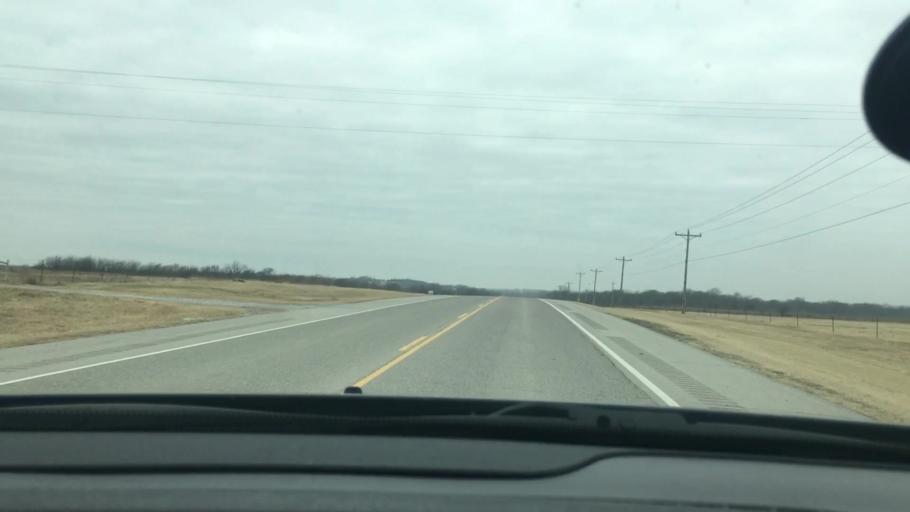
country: US
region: Oklahoma
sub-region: Murray County
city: Davis
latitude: 34.5214
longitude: -97.2967
